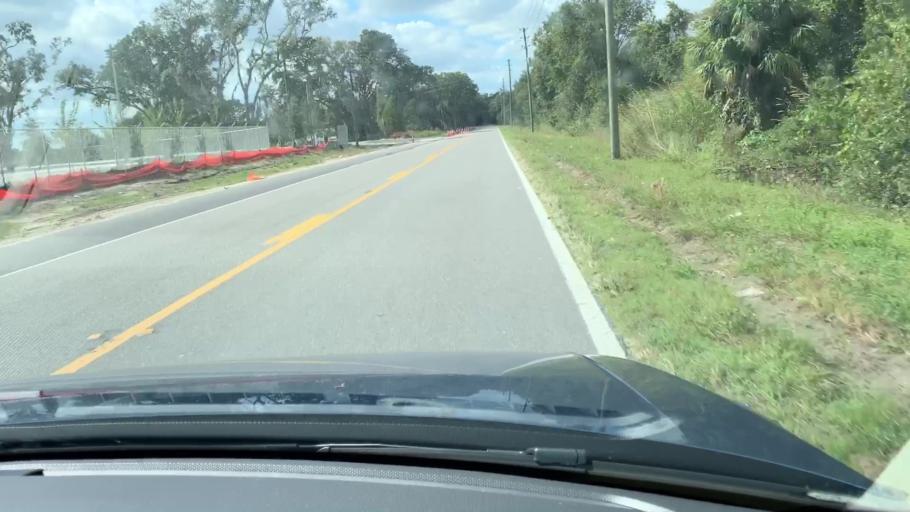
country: US
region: Florida
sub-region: Polk County
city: Winston
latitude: 28.0278
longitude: -82.0491
